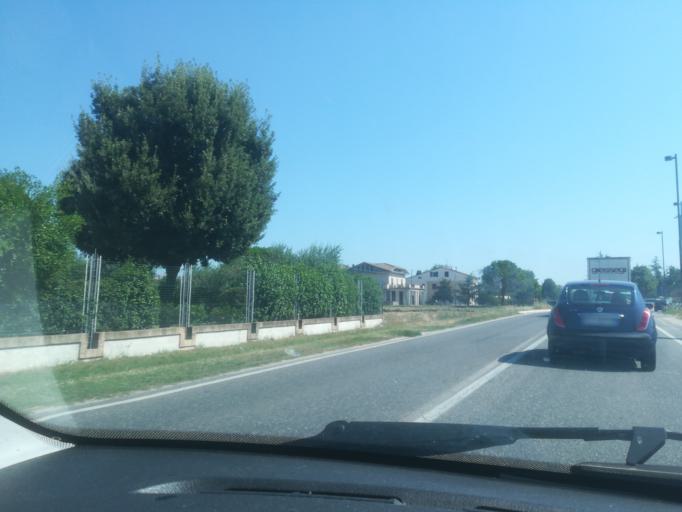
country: IT
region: The Marches
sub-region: Provincia di Macerata
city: Villa Potenza
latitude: 43.3386
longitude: 13.4356
